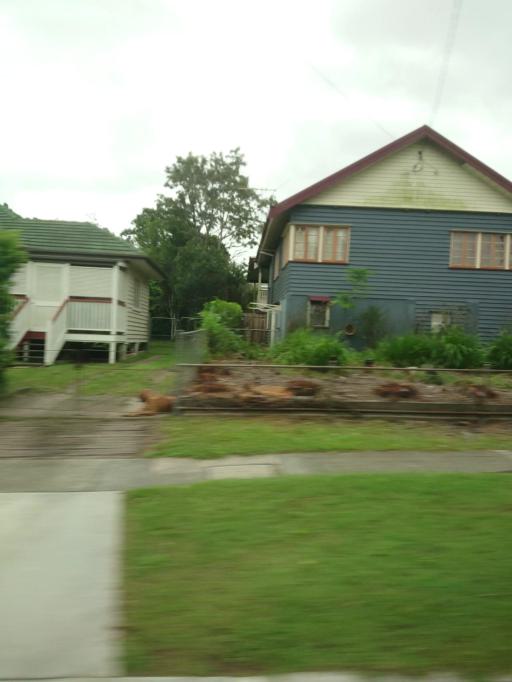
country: AU
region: Queensland
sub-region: Brisbane
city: Morningside
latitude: -27.4727
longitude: 153.0806
